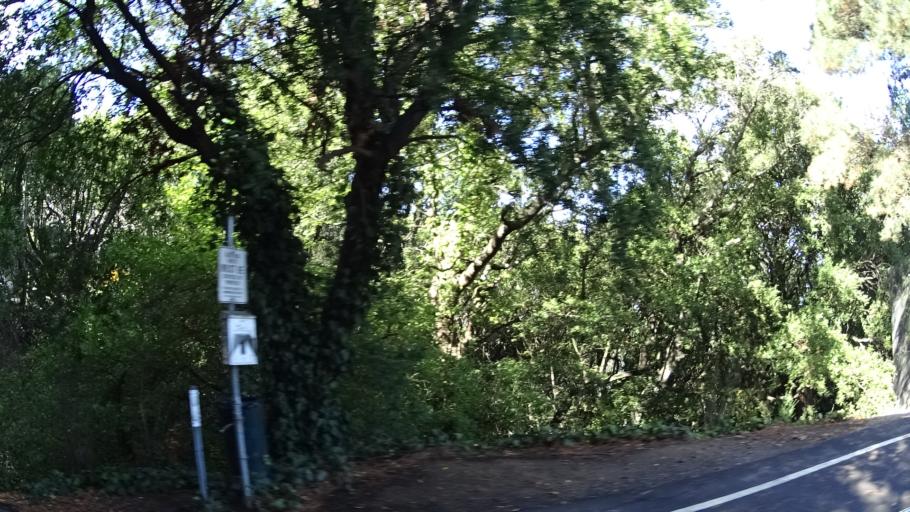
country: US
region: California
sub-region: San Mateo County
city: Brisbane
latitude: 37.6788
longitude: -122.4051
